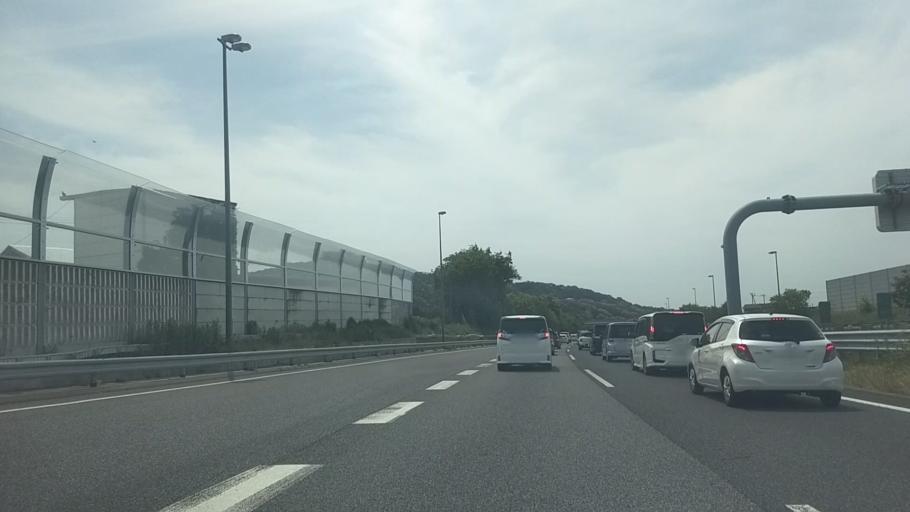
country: JP
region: Aichi
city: Shinshiro
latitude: 34.8219
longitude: 137.5493
